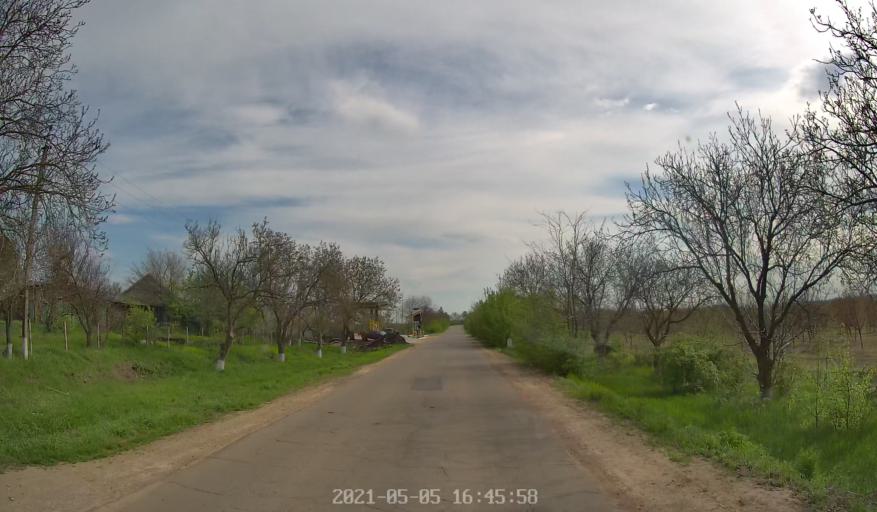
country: MD
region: Criuleni
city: Criuleni
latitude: 47.1045
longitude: 29.1925
